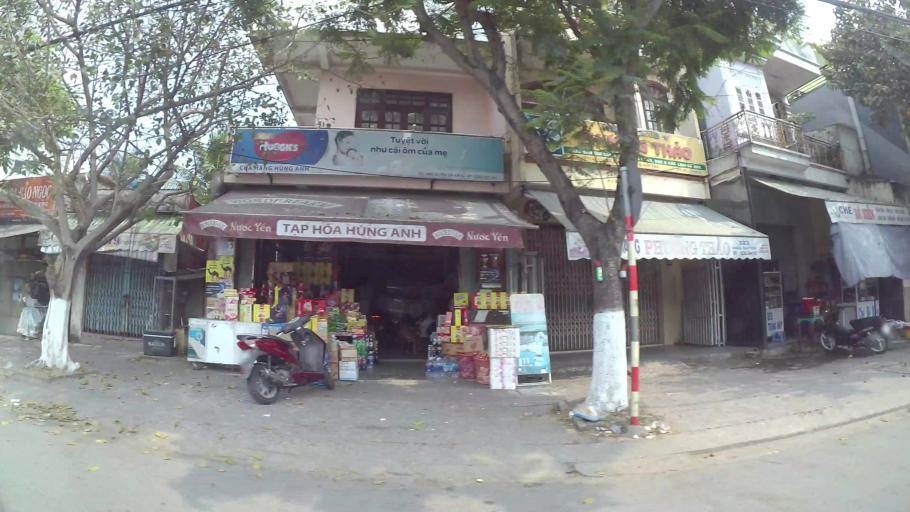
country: VN
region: Da Nang
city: Son Tra
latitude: 16.0870
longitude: 108.2412
